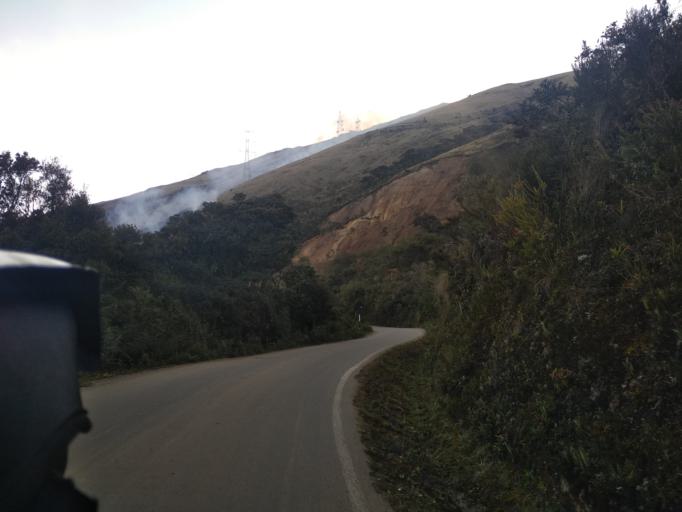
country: PE
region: Amazonas
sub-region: Provincia de Chachapoyas
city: Montevideo
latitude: -6.7190
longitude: -77.8738
